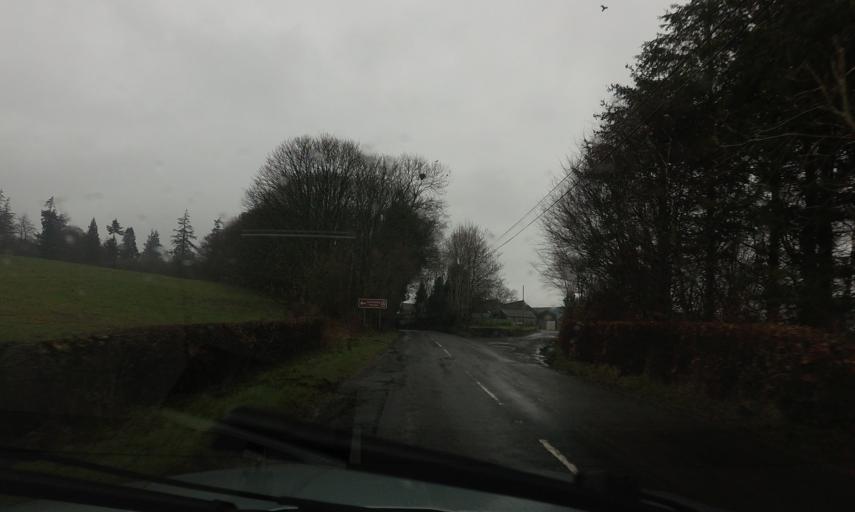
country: GB
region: Scotland
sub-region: Stirling
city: Balfron
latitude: 56.1530
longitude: -4.3620
